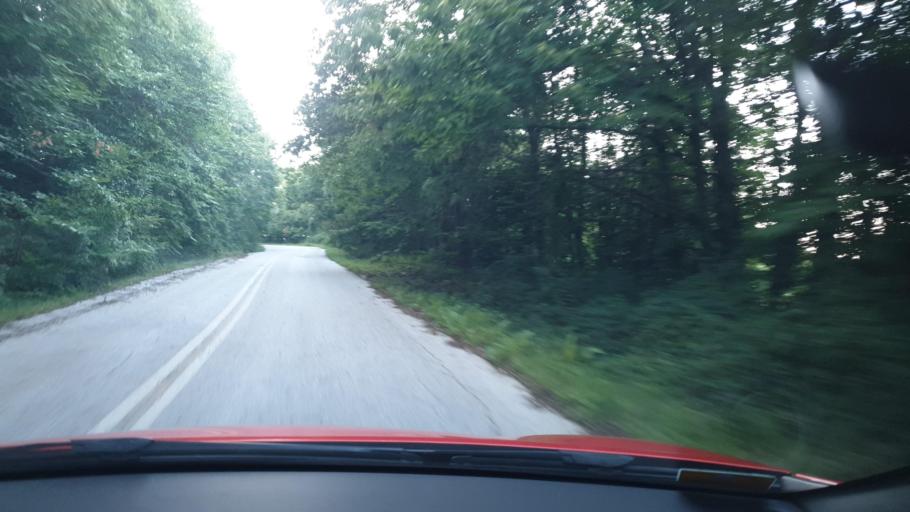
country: GR
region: Central Macedonia
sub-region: Nomos Chalkidikis
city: Galatista
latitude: 40.5073
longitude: 23.2613
